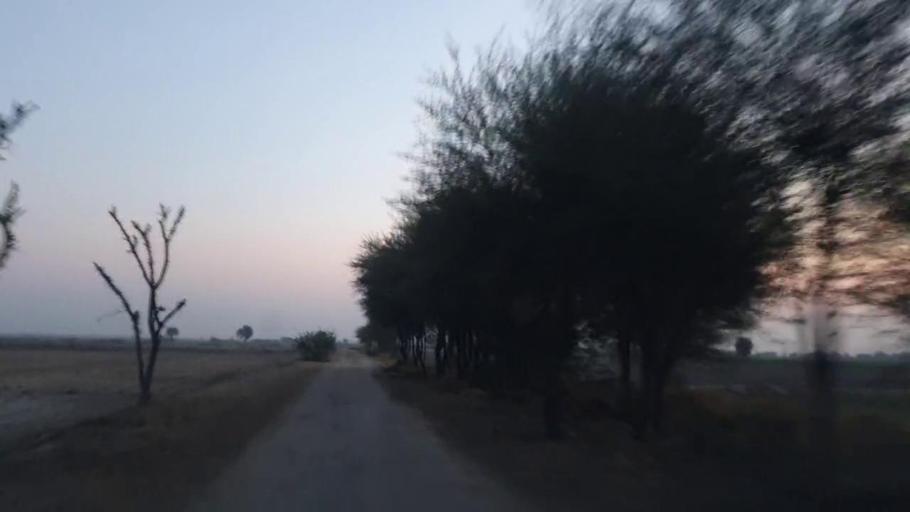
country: PK
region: Sindh
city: Naukot
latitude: 25.0195
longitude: 69.4118
